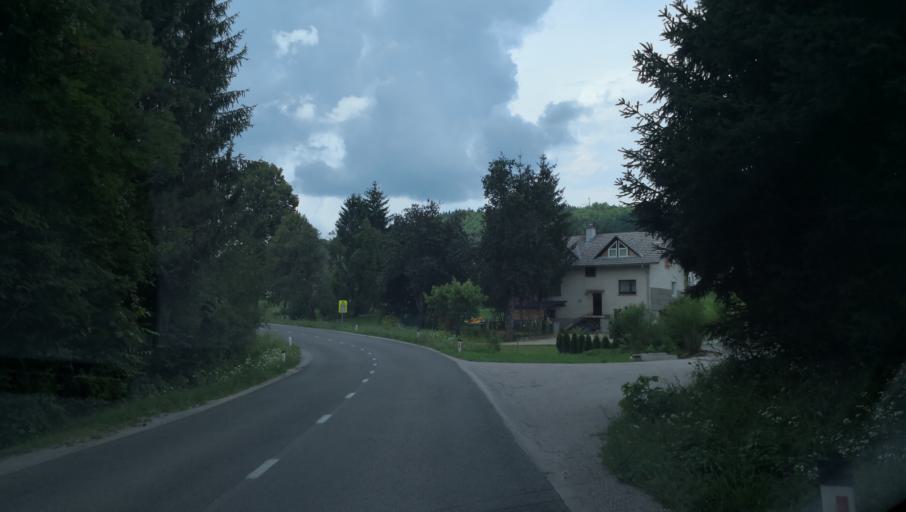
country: SI
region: Ivancna Gorica
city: Ivancna Gorica
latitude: 45.8684
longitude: 14.8257
